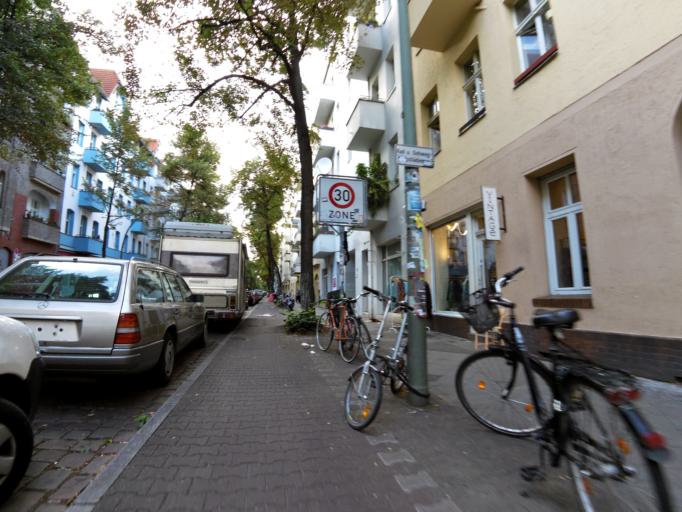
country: DE
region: Berlin
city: Berlin Treptow
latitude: 52.4832
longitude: 13.4415
